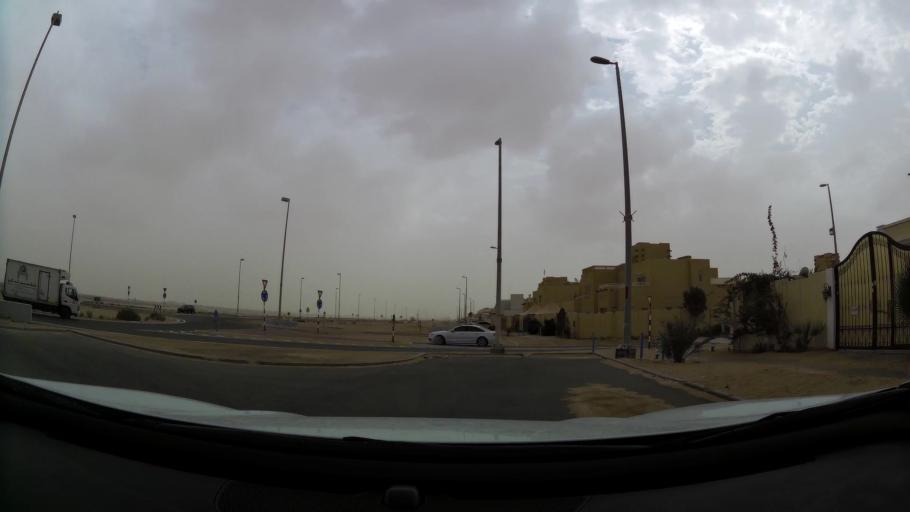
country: AE
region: Abu Dhabi
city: Abu Dhabi
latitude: 24.4605
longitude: 54.7168
